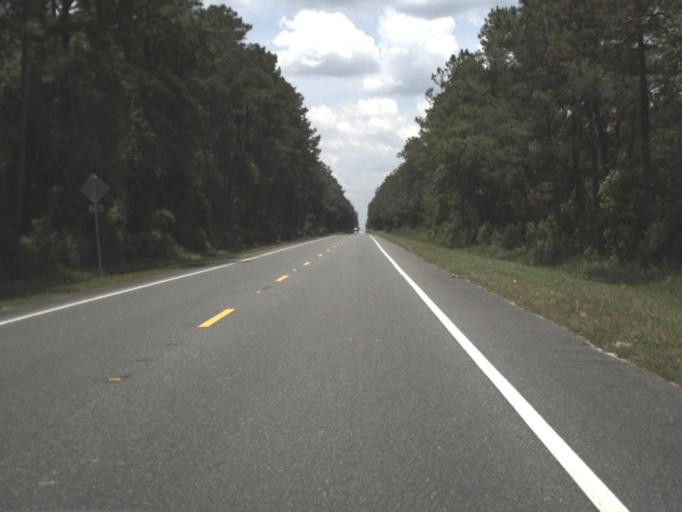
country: US
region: Florida
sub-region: Union County
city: Lake Butler
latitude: 30.0999
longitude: -82.4799
